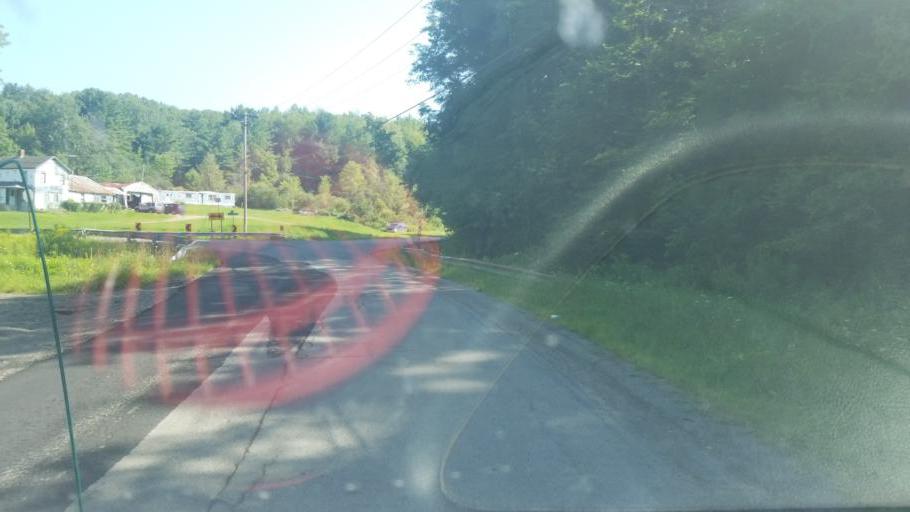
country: US
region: New York
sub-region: Allegany County
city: Bolivar
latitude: 42.0799
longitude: -78.0601
